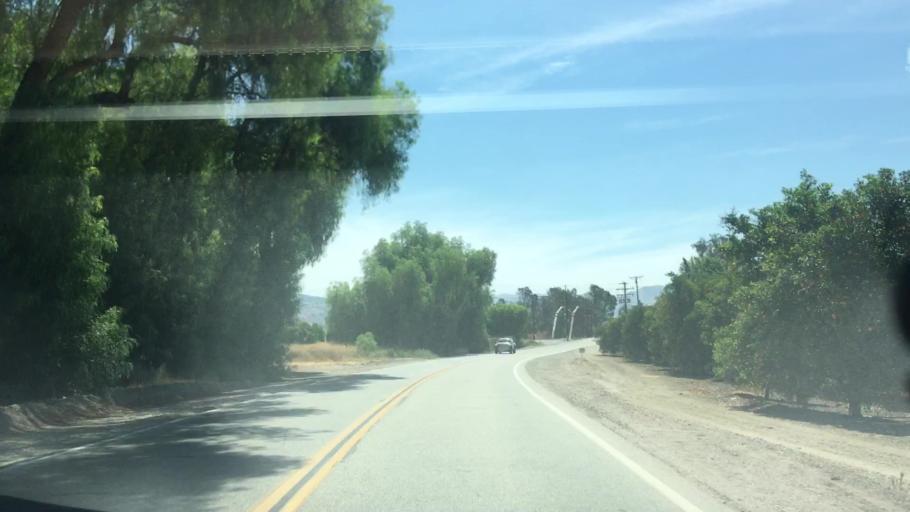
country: US
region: California
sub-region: Ventura County
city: Fillmore
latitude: 34.4083
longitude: -118.9368
